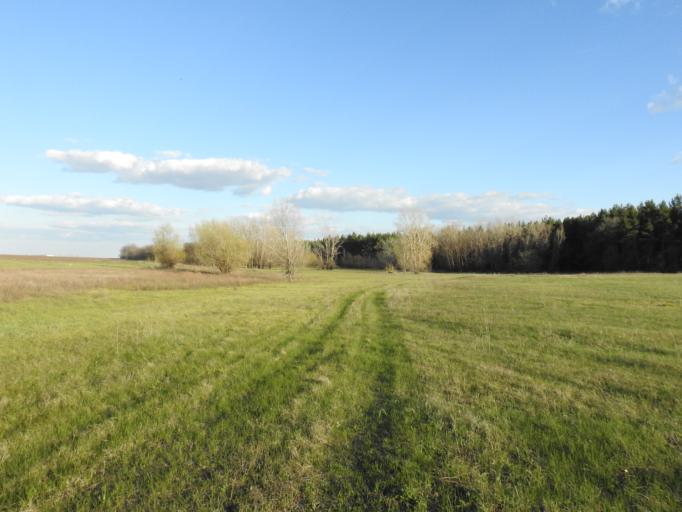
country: RU
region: Saratov
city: Krasnyy Yar
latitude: 51.5884
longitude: 46.5848
